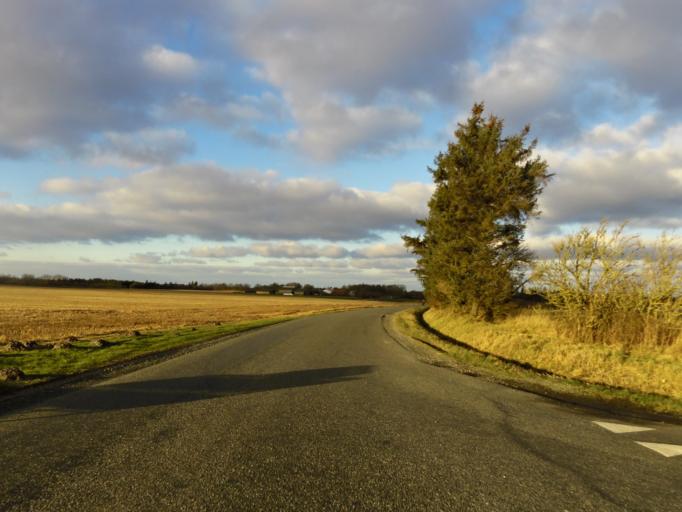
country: DK
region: South Denmark
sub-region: Esbjerg Kommune
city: Ribe
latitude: 55.3000
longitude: 8.8484
